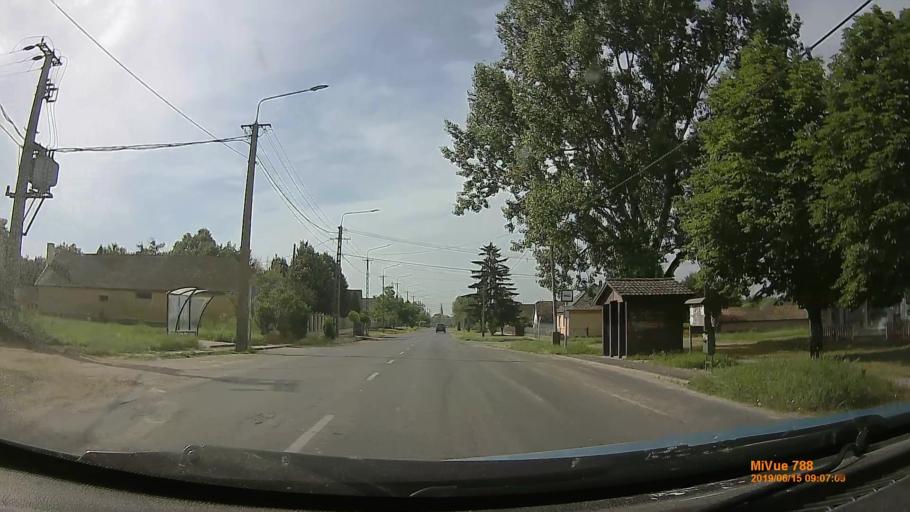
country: HU
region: Tolna
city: Iregszemcse
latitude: 46.7049
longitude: 18.1778
